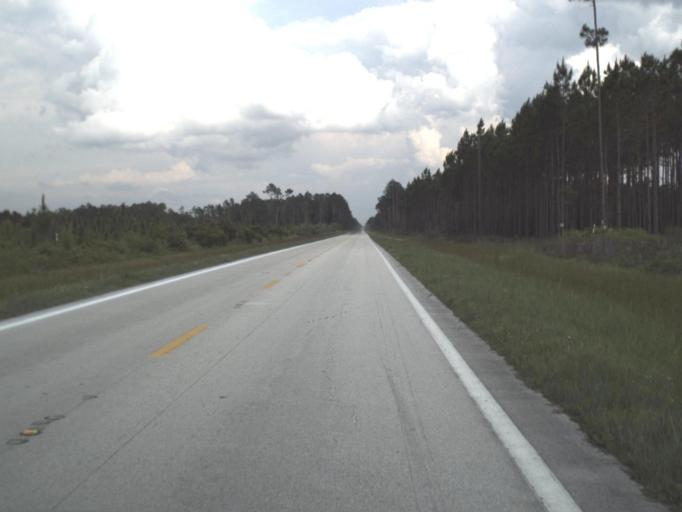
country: US
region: Florida
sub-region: Baker County
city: Macclenny
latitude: 30.5360
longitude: -82.3246
